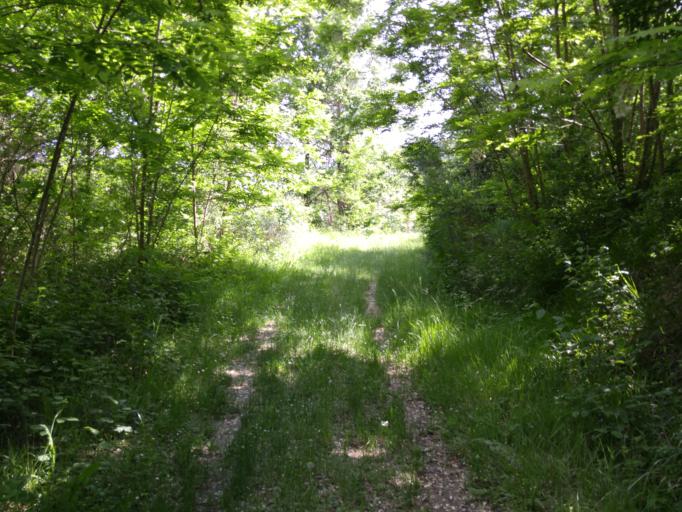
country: IT
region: The Marches
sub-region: Provincia di Pesaro e Urbino
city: Fermignano
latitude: 43.6978
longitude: 12.6272
